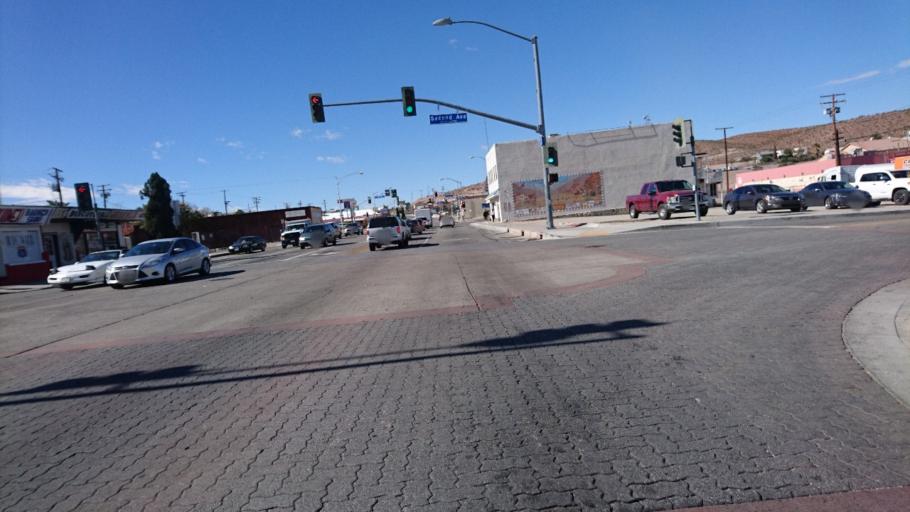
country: US
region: California
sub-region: San Bernardino County
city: Barstow
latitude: 34.8988
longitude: -117.0259
